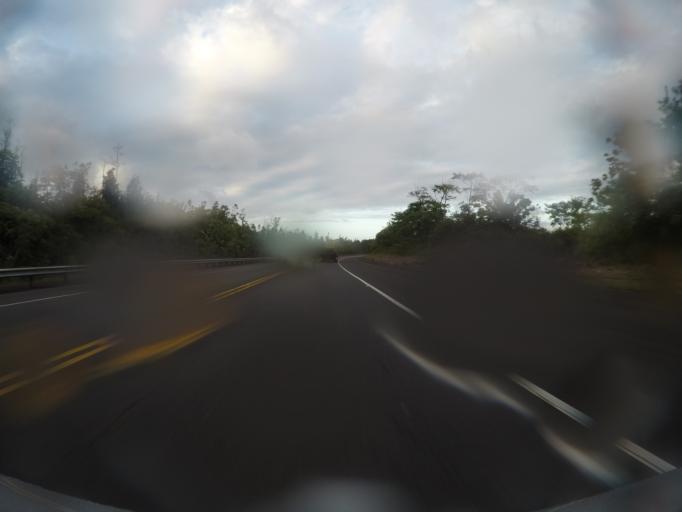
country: US
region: Hawaii
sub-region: Hawaii County
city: Hilo
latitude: 19.6900
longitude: -155.1155
